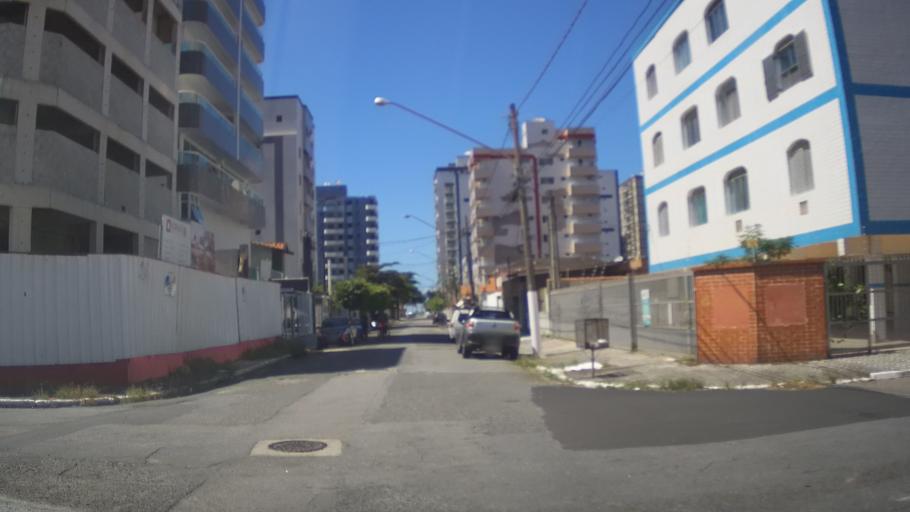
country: BR
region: Sao Paulo
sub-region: Praia Grande
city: Praia Grande
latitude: -24.0247
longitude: -46.4689
